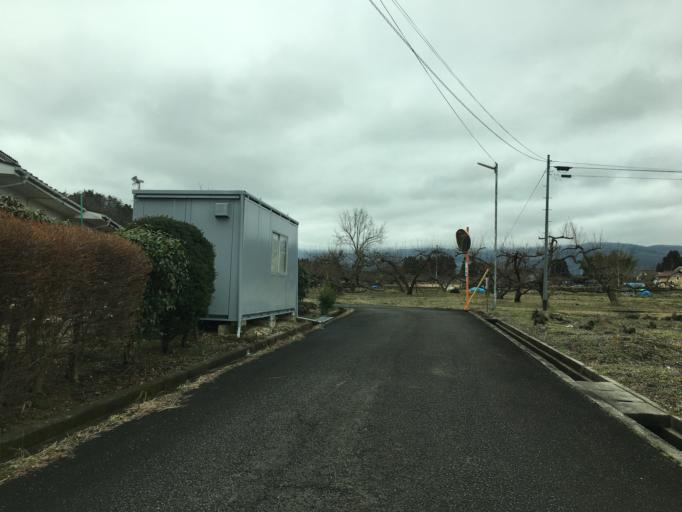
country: JP
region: Fukushima
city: Fukushima-shi
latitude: 37.7193
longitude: 140.4024
